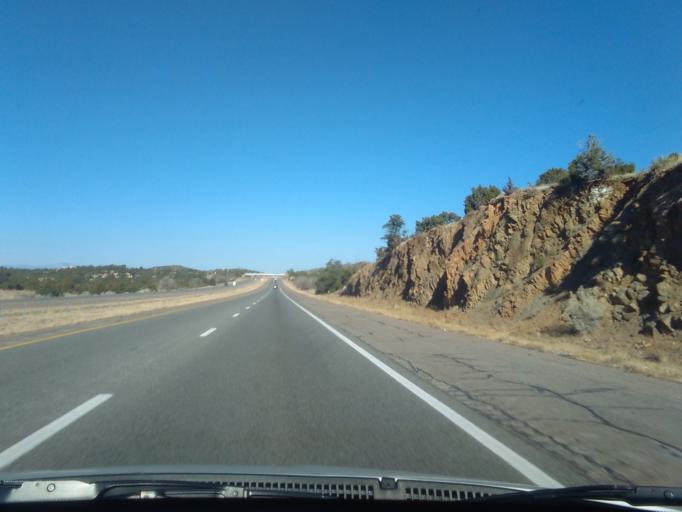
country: US
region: New Mexico
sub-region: Santa Fe County
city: Eldorado at Santa Fe
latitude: 35.5940
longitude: -105.9051
